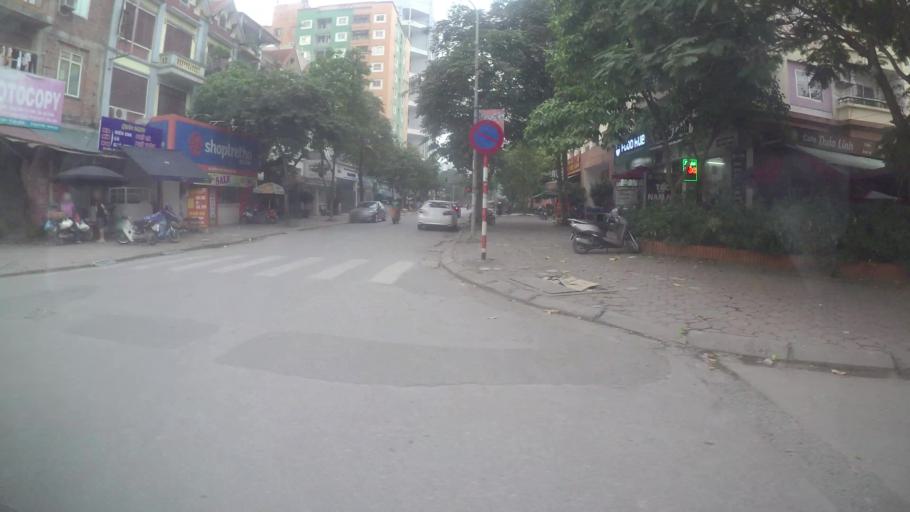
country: VN
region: Ha Noi
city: Cau Dien
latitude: 21.0326
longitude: 105.7640
